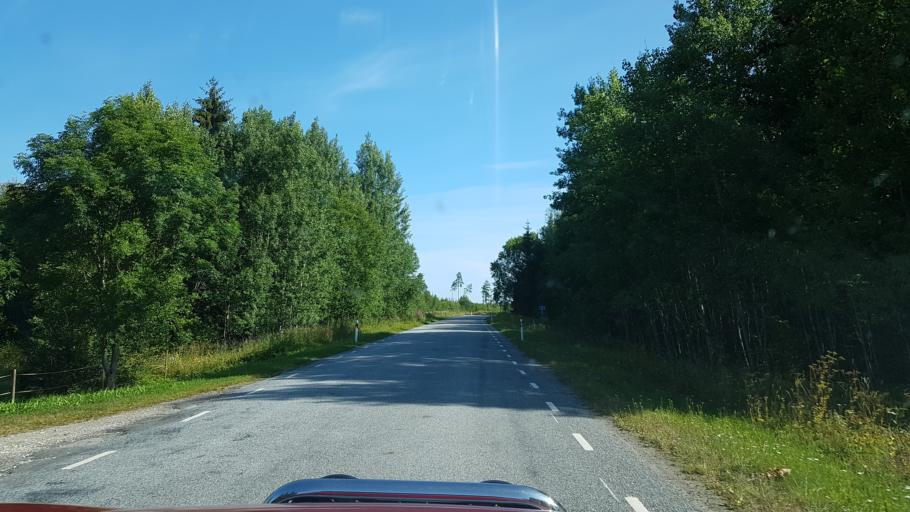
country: EE
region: Harju
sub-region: Raasiku vald
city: Raasiku
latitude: 59.2858
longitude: 25.1622
